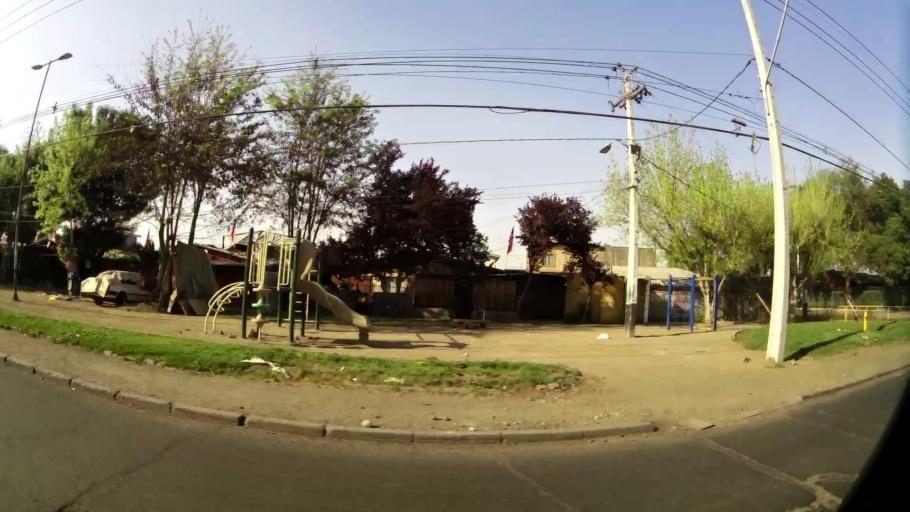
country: CL
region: Santiago Metropolitan
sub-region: Provincia de Santiago
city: Lo Prado
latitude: -33.4146
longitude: -70.7650
